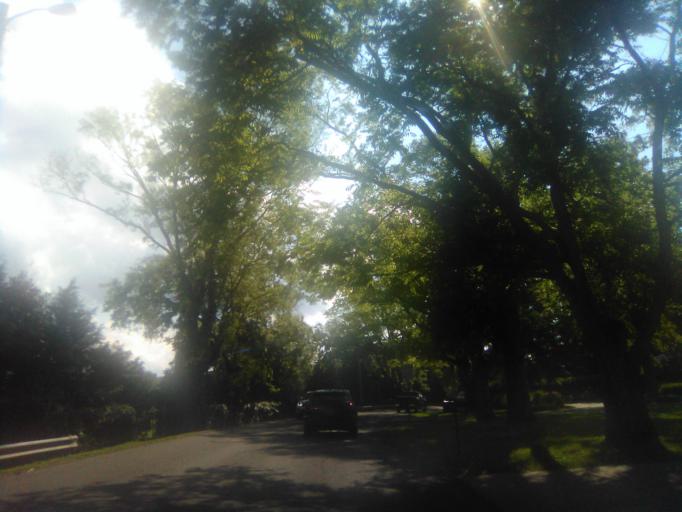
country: US
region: Tennessee
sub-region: Davidson County
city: Belle Meade
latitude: 36.0965
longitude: -86.8620
